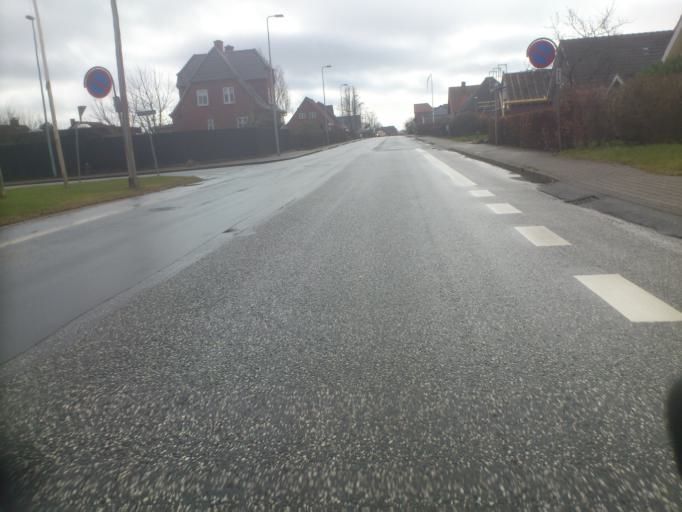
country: DK
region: South Denmark
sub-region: Fredericia Kommune
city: Fredericia
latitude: 55.5809
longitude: 9.7538
